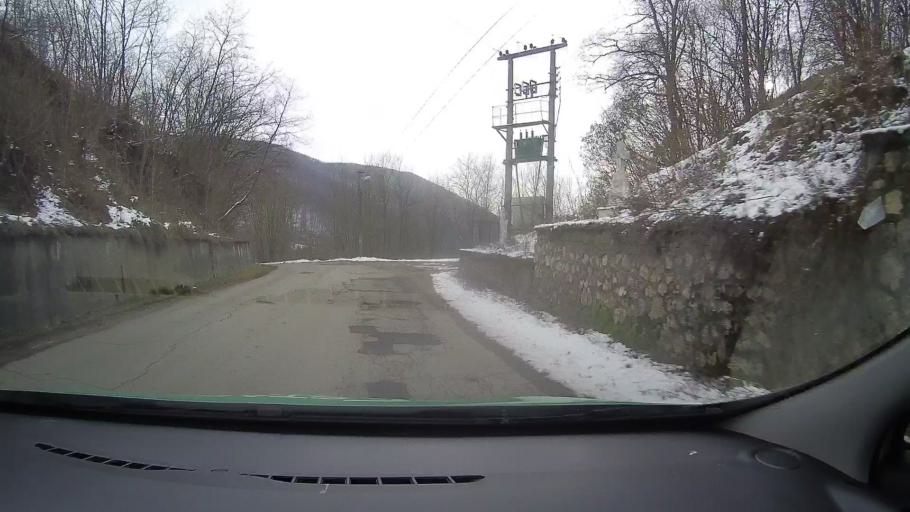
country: RO
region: Hunedoara
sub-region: Comuna Balsa
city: Balsa
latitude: 46.0178
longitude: 23.1471
